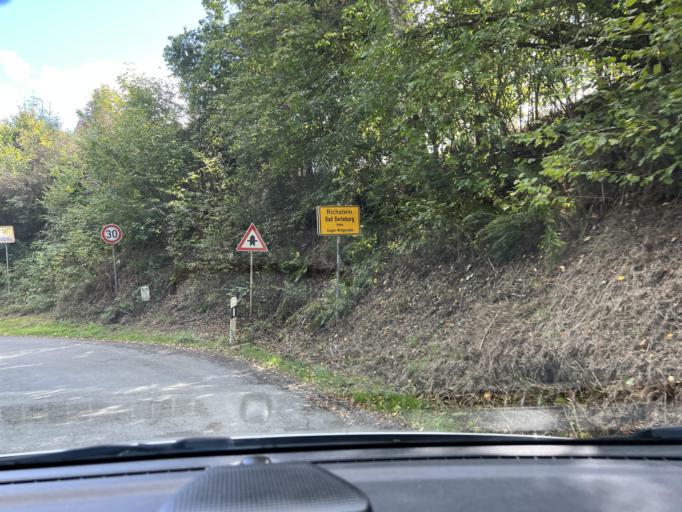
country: DE
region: North Rhine-Westphalia
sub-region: Regierungsbezirk Arnsberg
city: Bad Laasphe
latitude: 50.9835
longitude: 8.4625
